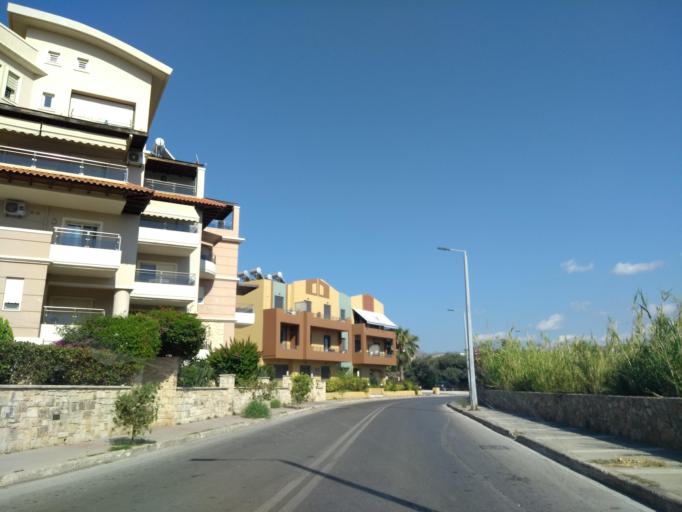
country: GR
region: Crete
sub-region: Nomos Chanias
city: Perivolia
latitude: 35.5089
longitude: 24.0031
